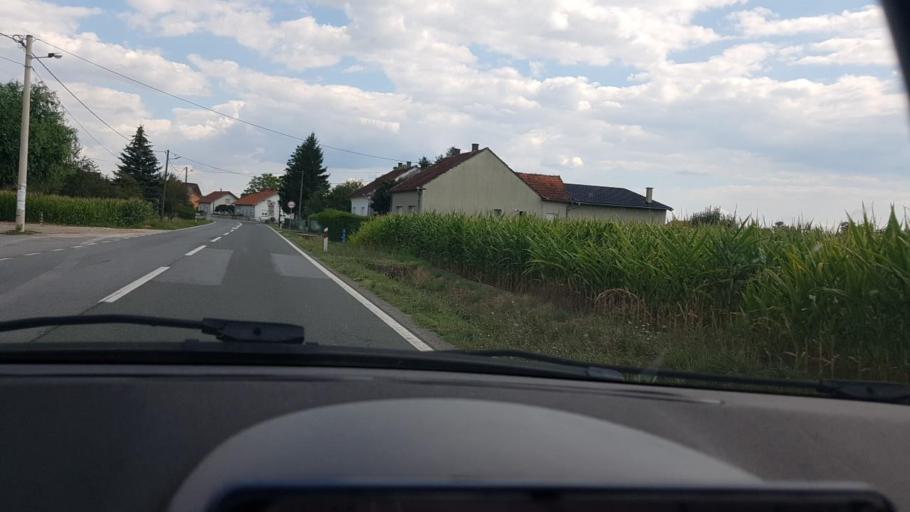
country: HR
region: Bjelovarsko-Bilogorska
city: Zdralovi
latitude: 45.8574
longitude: 16.9243
